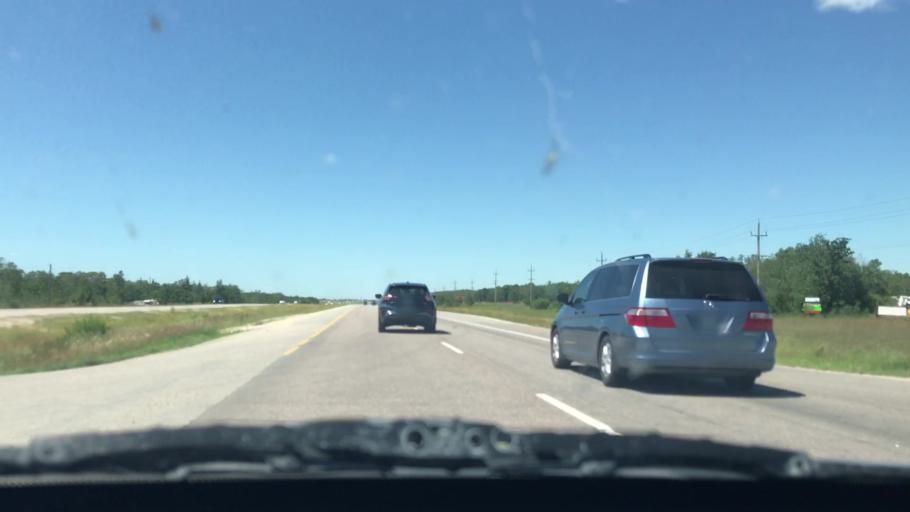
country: CA
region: Manitoba
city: Steinbach
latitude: 49.6804
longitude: -96.5939
